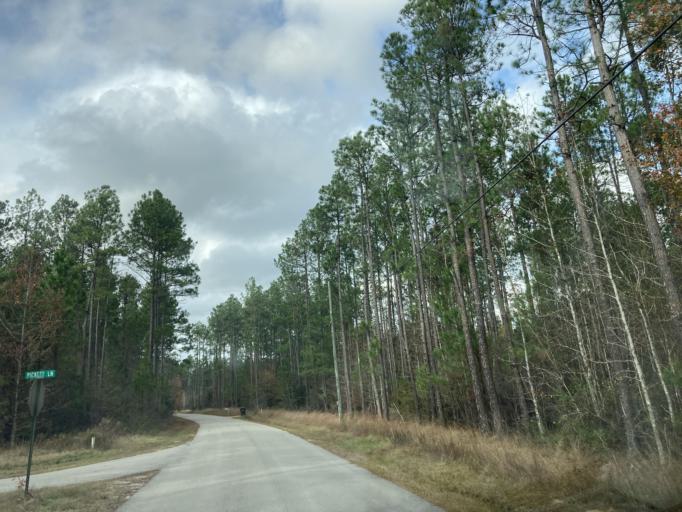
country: US
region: Mississippi
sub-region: Lamar County
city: Purvis
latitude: 31.1755
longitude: -89.5780
